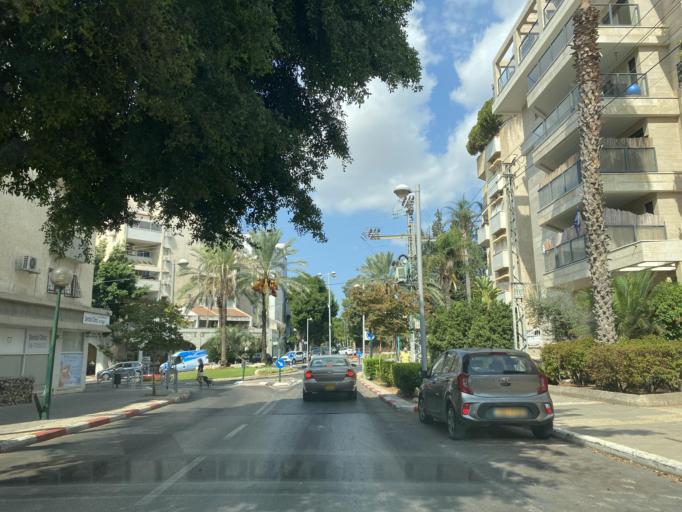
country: IL
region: Central District
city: Kfar Saba
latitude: 32.1779
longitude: 34.9099
